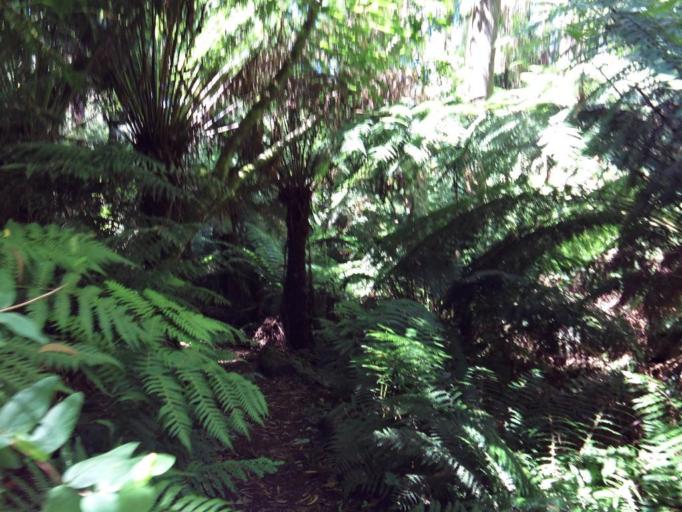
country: AU
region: Victoria
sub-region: Yarra Ranges
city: Mount Dandenong
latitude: -37.8331
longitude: 145.3657
